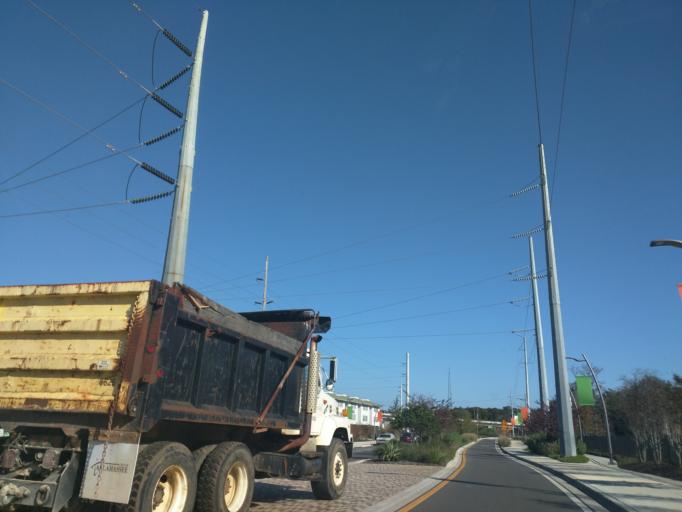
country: US
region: Florida
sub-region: Leon County
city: Tallahassee
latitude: 30.4316
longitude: -84.2875
